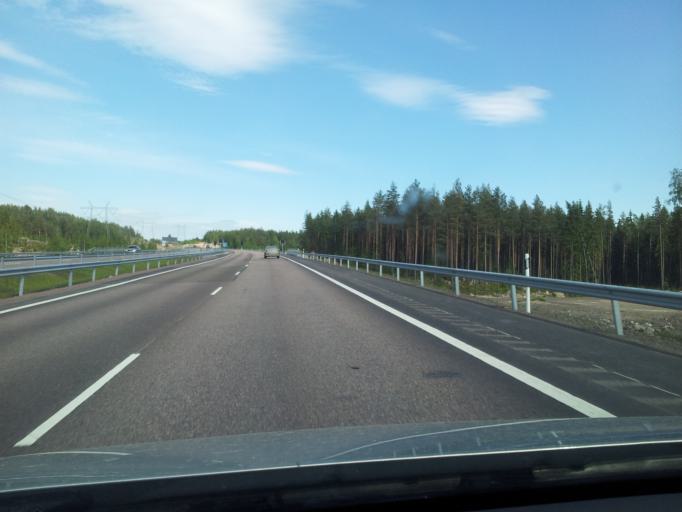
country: FI
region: Uusimaa
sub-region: Loviisa
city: Ruotsinpyhtaeae
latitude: 60.4873
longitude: 26.3875
